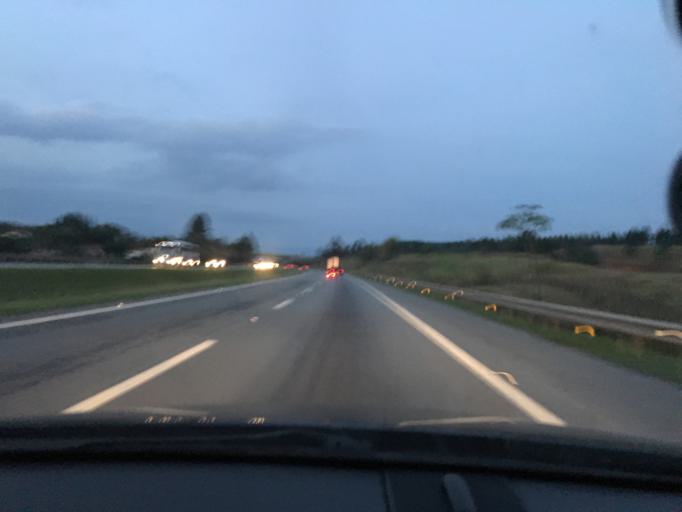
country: BR
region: Sao Paulo
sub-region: Santa Isabel
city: Santa Isabel
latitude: -23.4109
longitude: -46.1875
